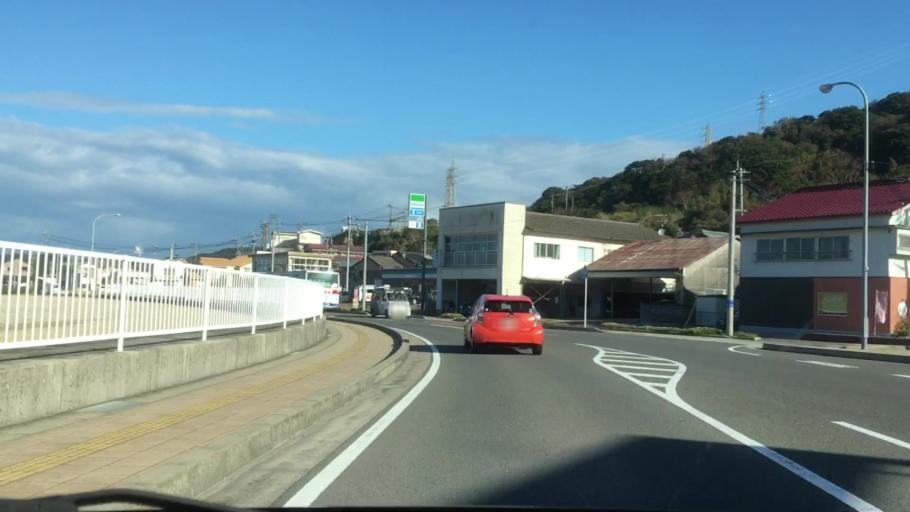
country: JP
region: Nagasaki
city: Togitsu
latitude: 32.9348
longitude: 129.6407
